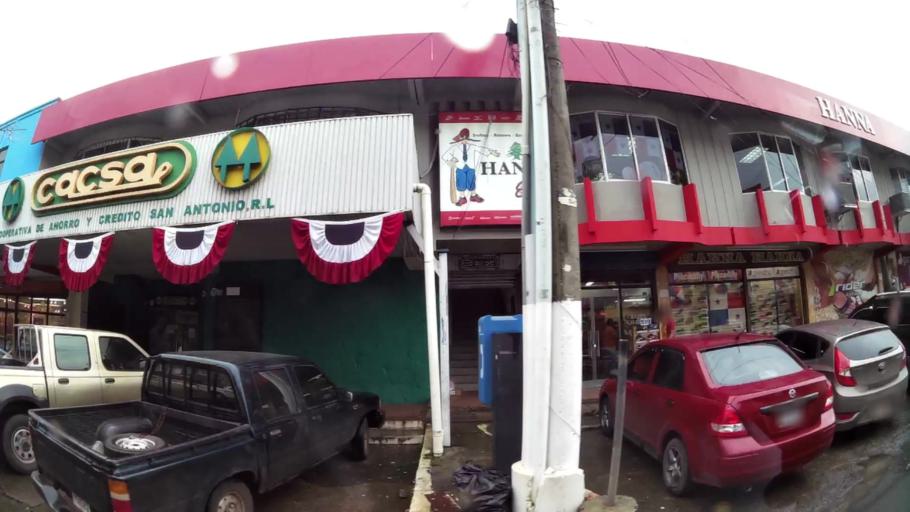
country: PA
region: Veraguas
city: Santiago de Veraguas
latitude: 8.0971
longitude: -80.9818
